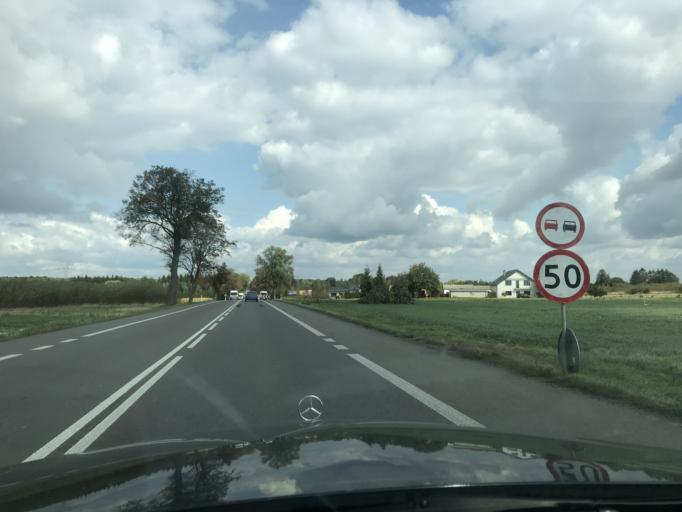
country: PL
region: Lublin Voivodeship
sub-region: Powiat lubelski
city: Kozubszczyzna
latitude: 51.1902
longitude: 22.4354
